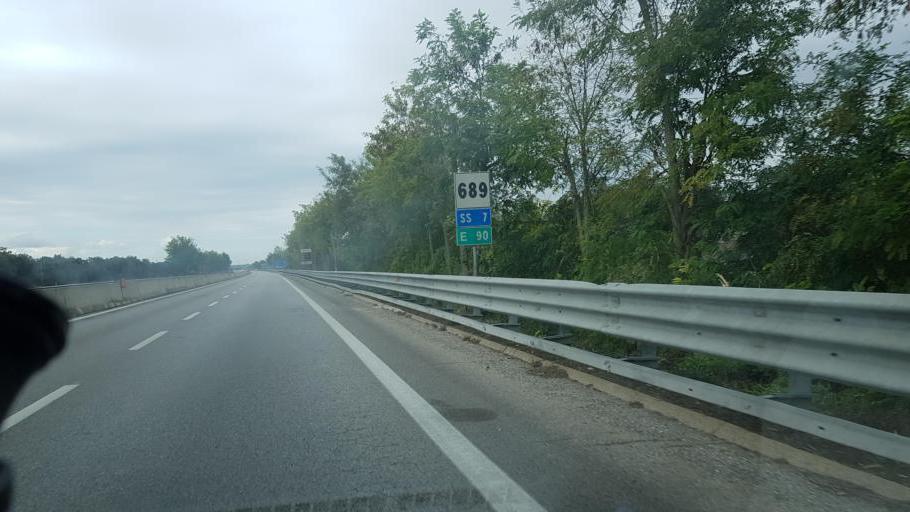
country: IT
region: Apulia
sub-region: Provincia di Brindisi
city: Oria
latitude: 40.5415
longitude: 17.6685
